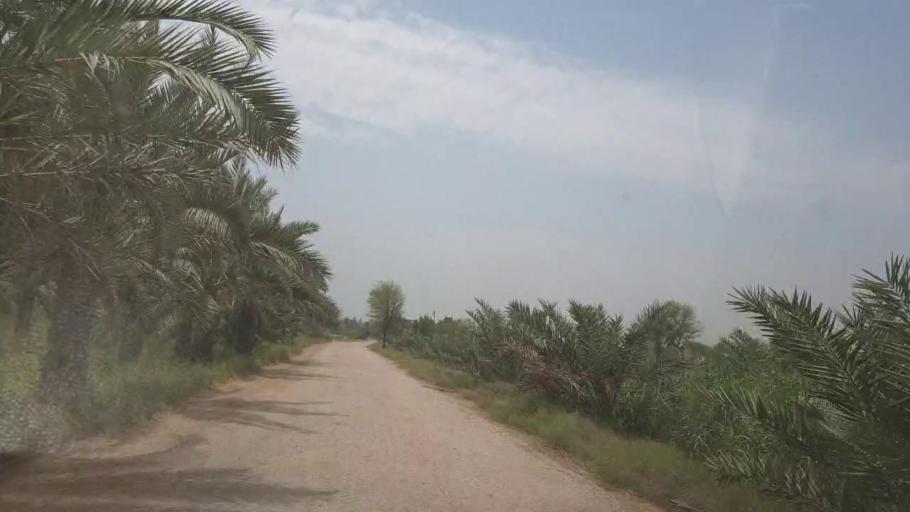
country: PK
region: Sindh
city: Kot Diji
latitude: 27.4422
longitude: 68.6806
